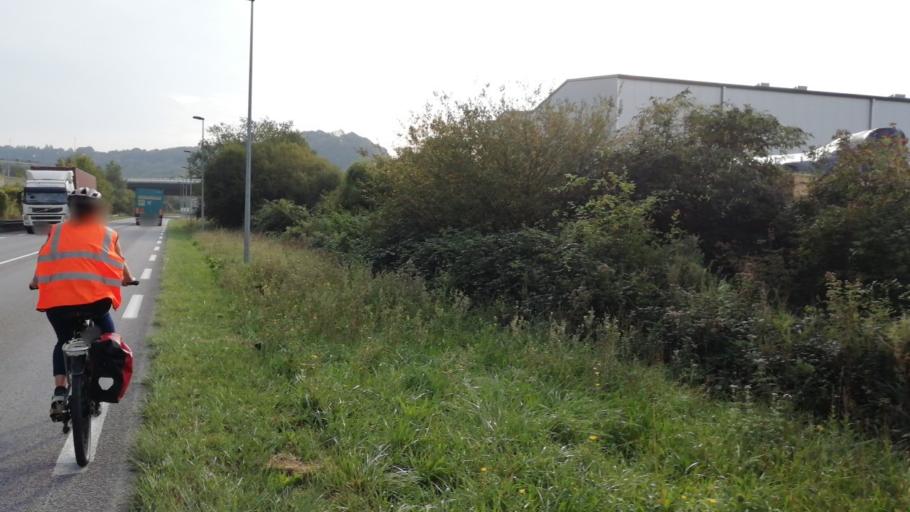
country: FR
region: Haute-Normandie
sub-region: Departement de la Seine-Maritime
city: Rogerville
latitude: 49.4967
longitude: 0.2648
